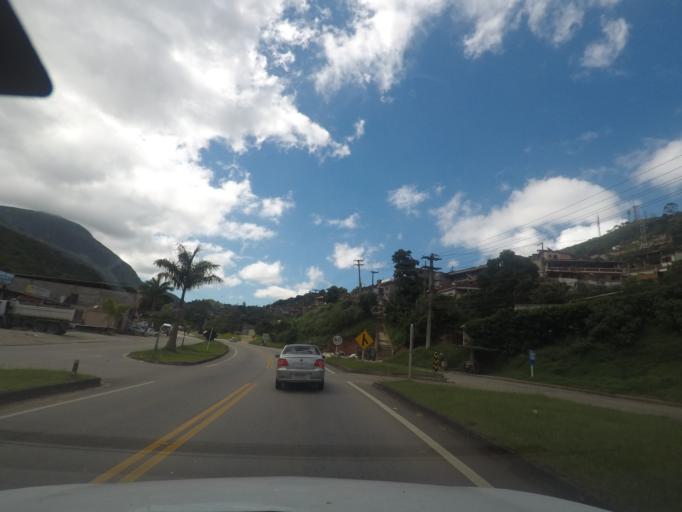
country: BR
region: Rio de Janeiro
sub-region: Teresopolis
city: Teresopolis
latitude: -22.3991
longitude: -42.9551
